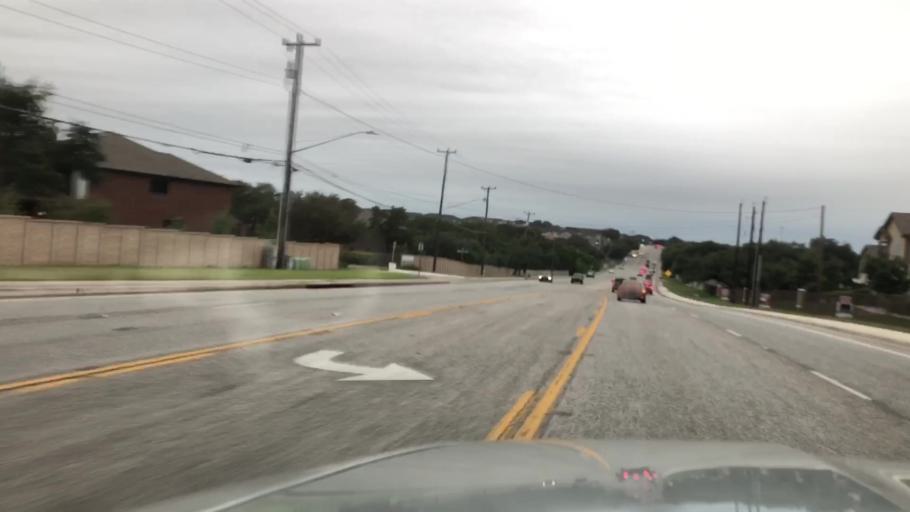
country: US
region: Texas
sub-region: Bexar County
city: Leon Valley
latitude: 29.5192
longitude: -98.6083
